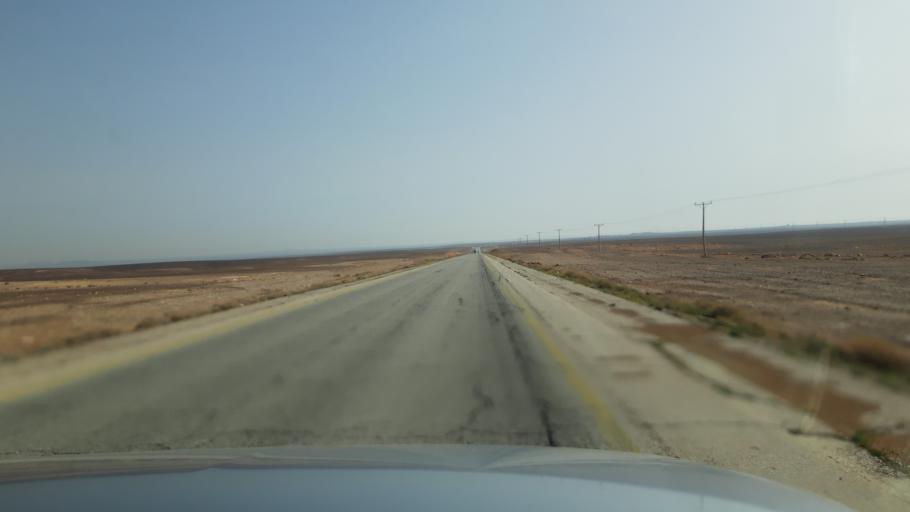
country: JO
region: Amman
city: Al Azraq ash Shamali
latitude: 31.8552
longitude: 36.6875
